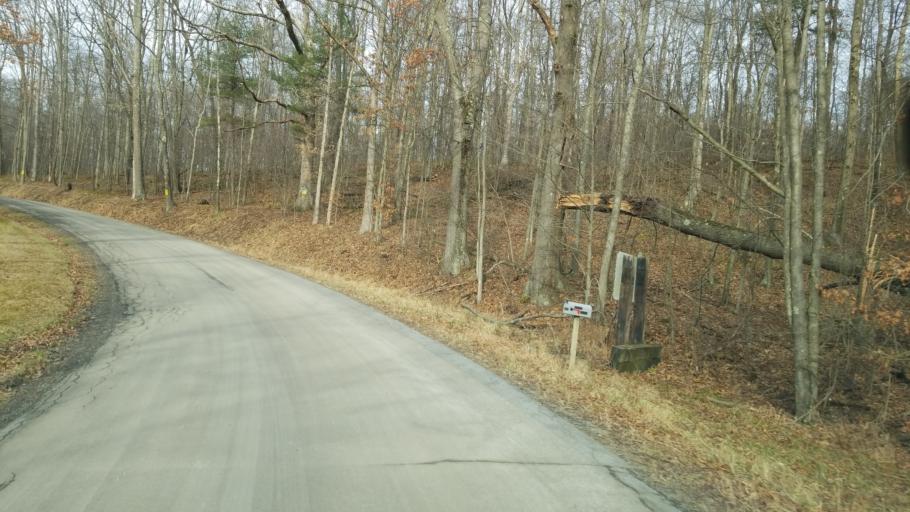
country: US
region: Pennsylvania
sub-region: Jefferson County
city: Punxsutawney
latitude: 40.8509
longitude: -79.0080
